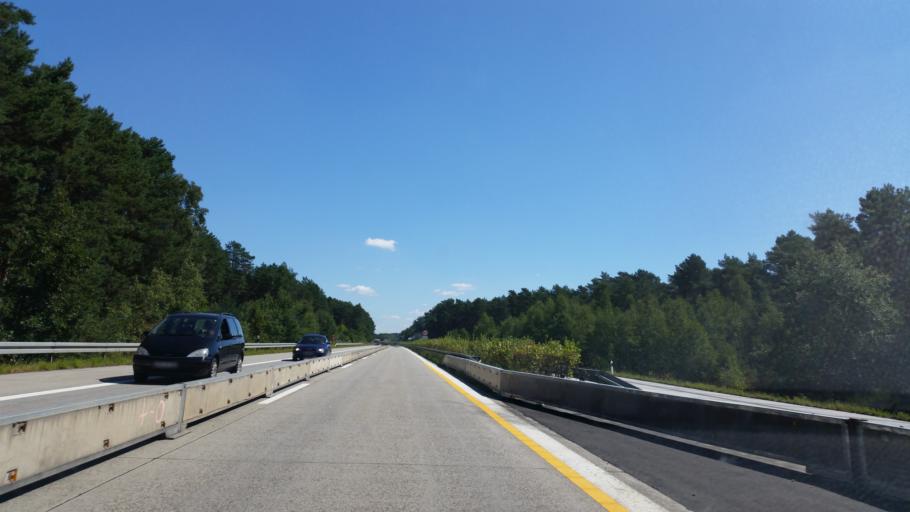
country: DE
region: Brandenburg
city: Cottbus
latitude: 51.7078
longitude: 14.4341
